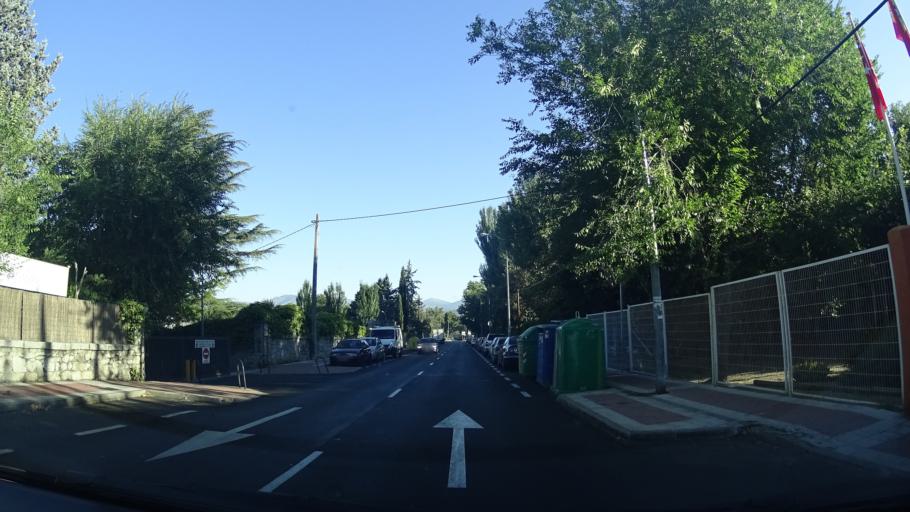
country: ES
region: Madrid
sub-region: Provincia de Madrid
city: Collado-Villalba
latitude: 40.6360
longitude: -4.0031
